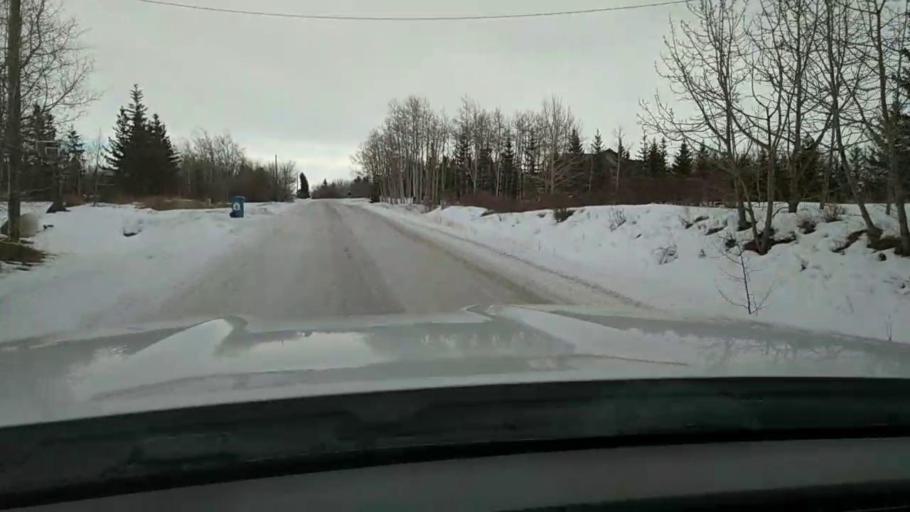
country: CA
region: Alberta
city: Cochrane
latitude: 51.1976
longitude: -114.2788
